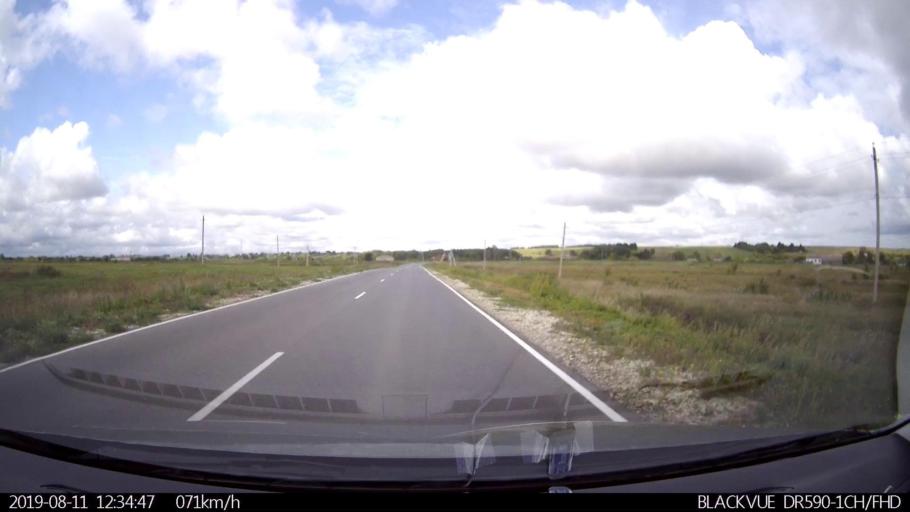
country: RU
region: Ulyanovsk
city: Ignatovka
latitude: 53.8195
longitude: 47.8382
